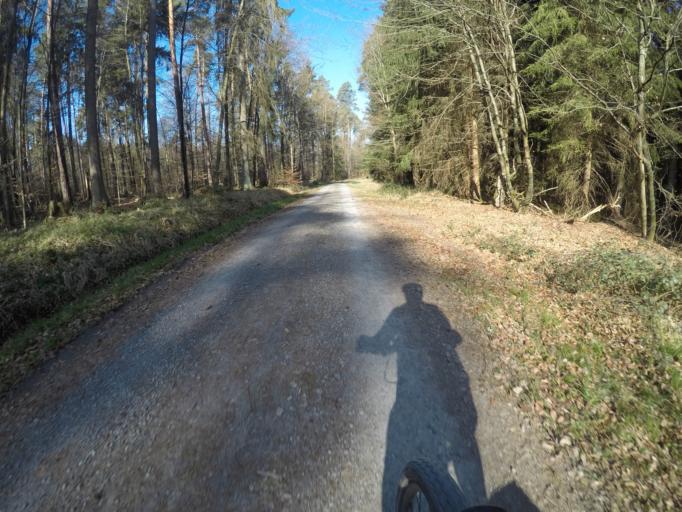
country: DE
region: Baden-Wuerttemberg
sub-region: Tuebingen Region
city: Dettenhausen
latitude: 48.6049
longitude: 9.1195
